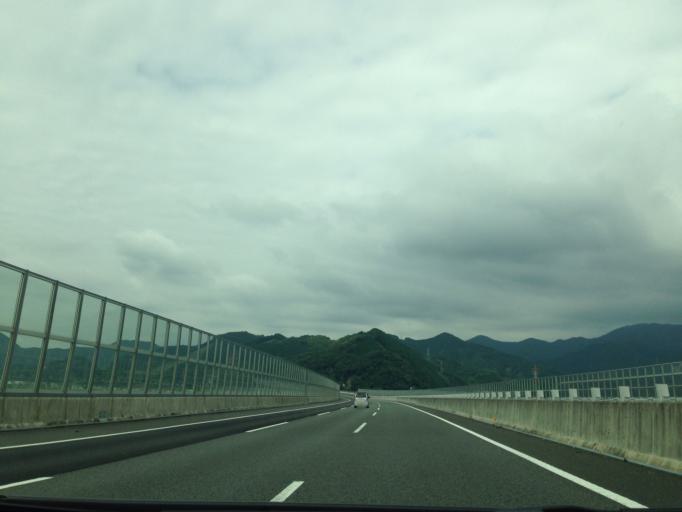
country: JP
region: Shizuoka
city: Shizuoka-shi
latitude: 35.0423
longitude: 138.3818
